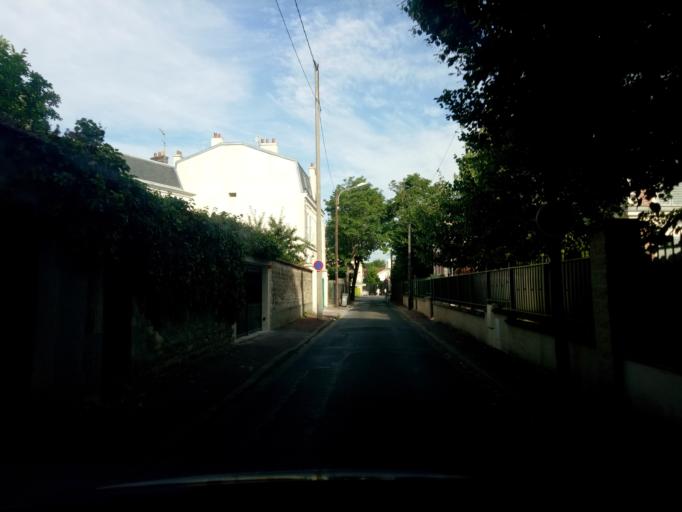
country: FR
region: Ile-de-France
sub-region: Departement des Yvelines
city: Chatou
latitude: 48.8847
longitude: 2.1557
